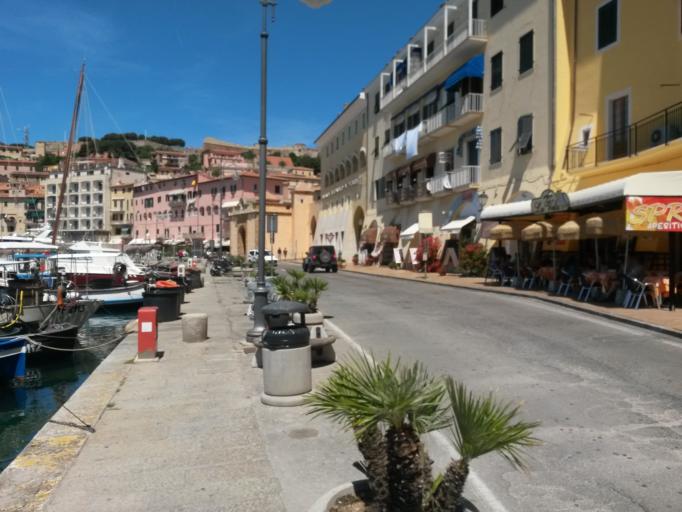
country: IT
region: Tuscany
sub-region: Provincia di Livorno
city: Portoferraio
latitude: 42.8138
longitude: 10.3318
